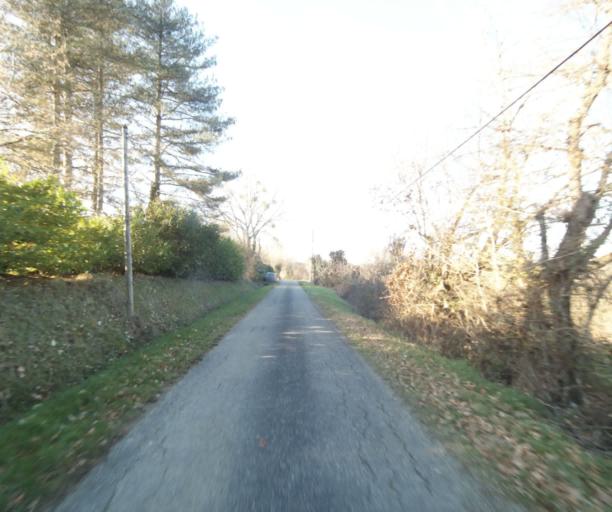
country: FR
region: Midi-Pyrenees
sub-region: Departement du Tarn-et-Garonne
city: Moissac
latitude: 44.1422
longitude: 1.0705
